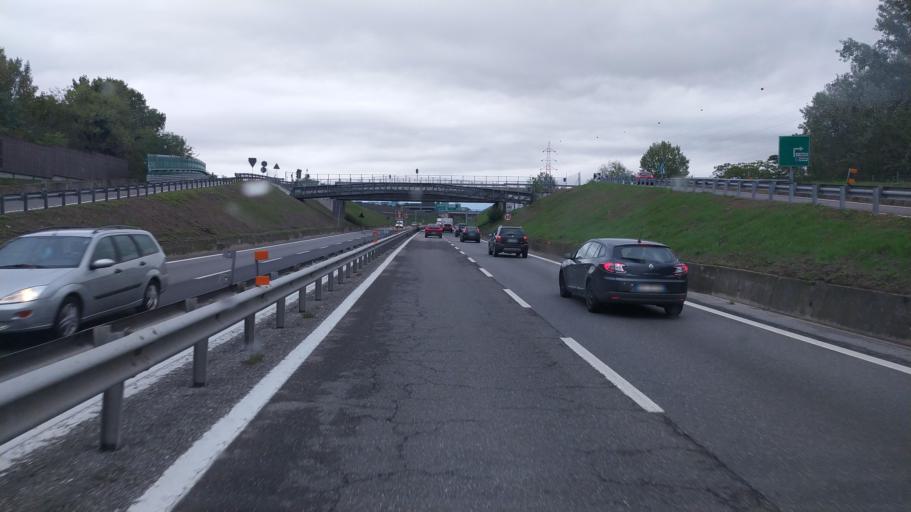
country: IT
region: Lombardy
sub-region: Provincia di Pavia
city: Pavia
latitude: 45.1981
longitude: 9.1376
